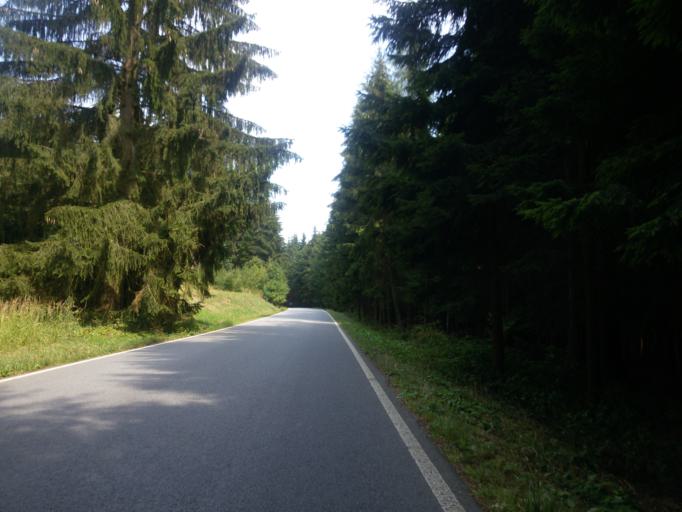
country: CZ
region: South Moravian
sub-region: Okres Brno-Venkov
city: Lomnice
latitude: 49.4597
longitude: 16.4420
